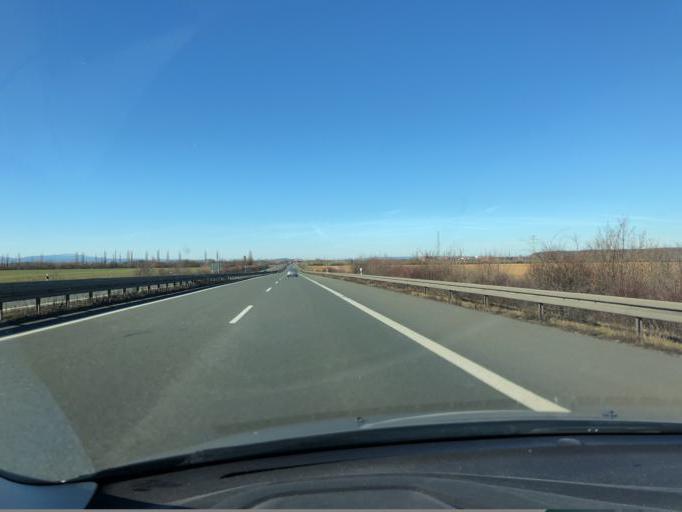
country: DE
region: Saxony-Anhalt
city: Frose
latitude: 51.7806
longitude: 11.3728
